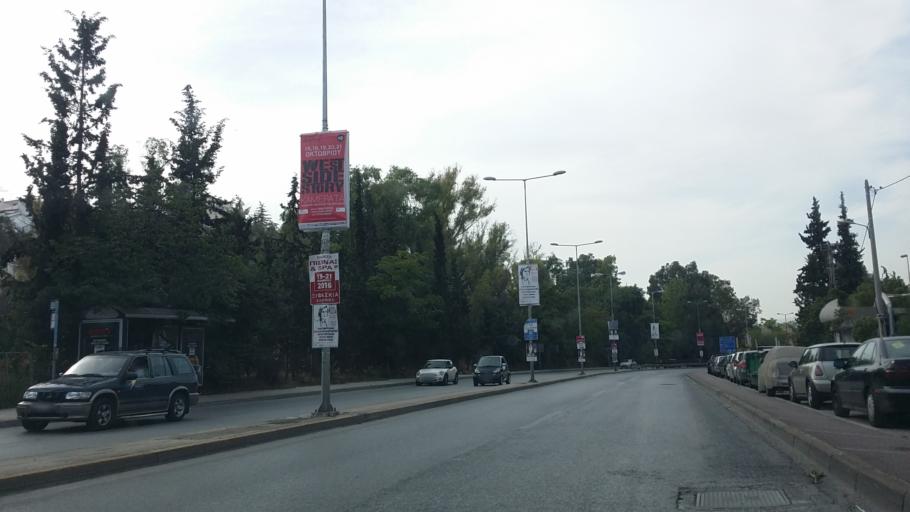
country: GR
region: Attica
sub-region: Nomarchia Athinas
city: Filothei
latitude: 38.0324
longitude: 23.7751
